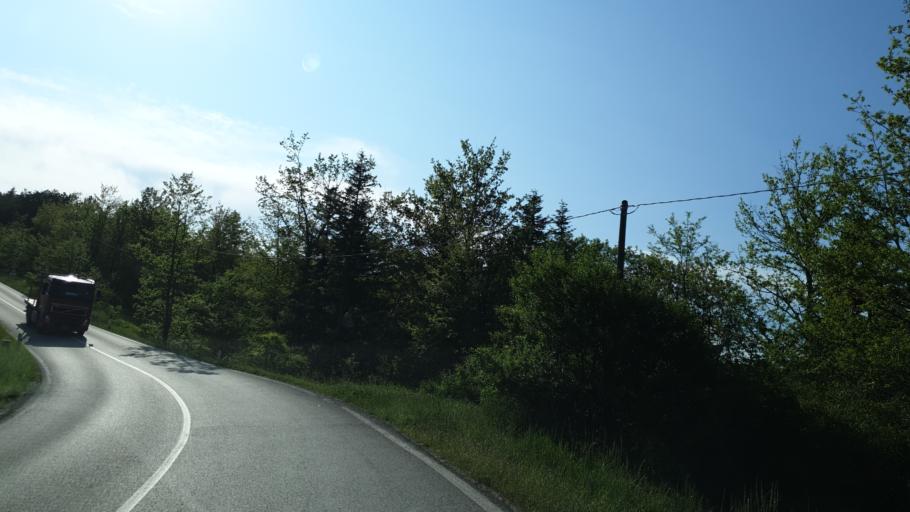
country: IT
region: Tuscany
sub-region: Province of Arezzo
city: Montemignaio
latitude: 43.7882
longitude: 11.6343
